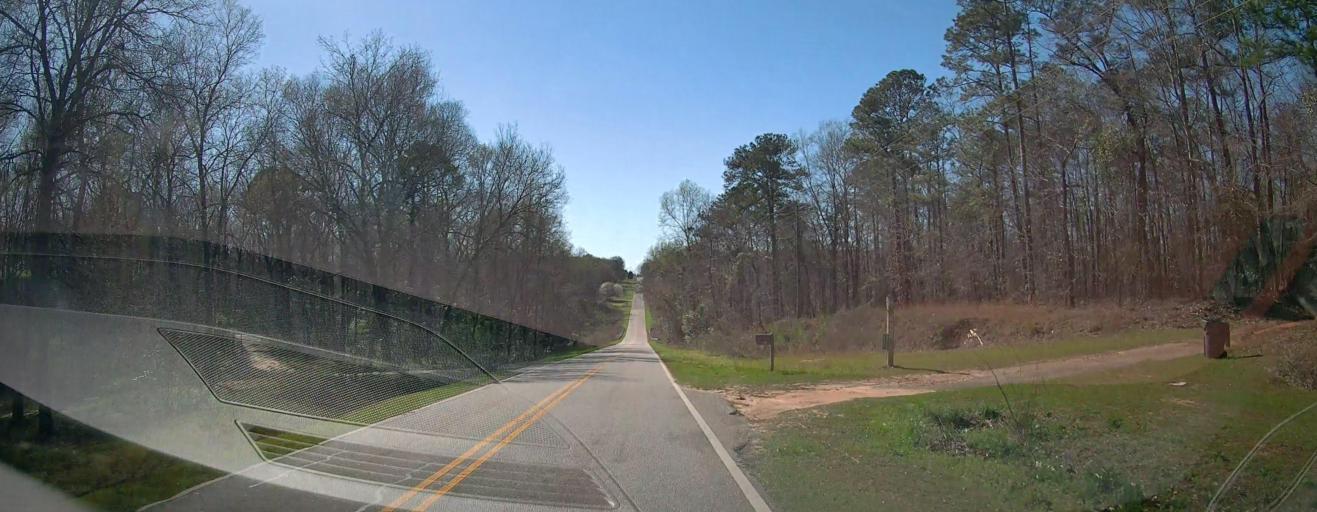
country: US
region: Georgia
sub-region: Peach County
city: Byron
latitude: 32.6442
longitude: -83.8334
